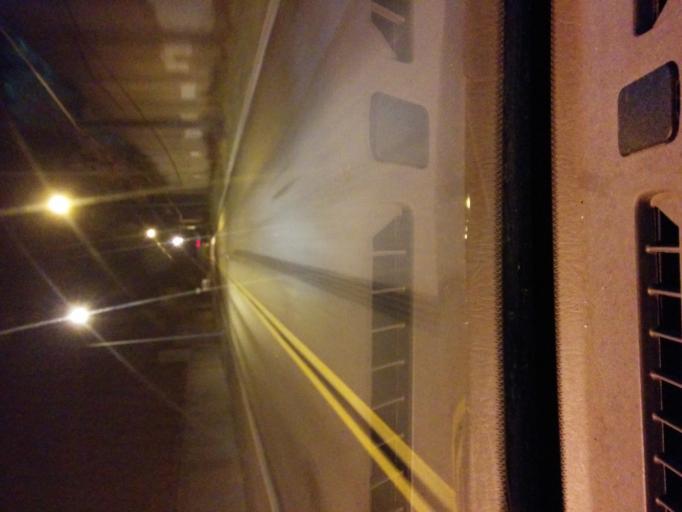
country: US
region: Pennsylvania
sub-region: Allegheny County
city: Mount Oliver
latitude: 40.4194
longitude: -79.9575
